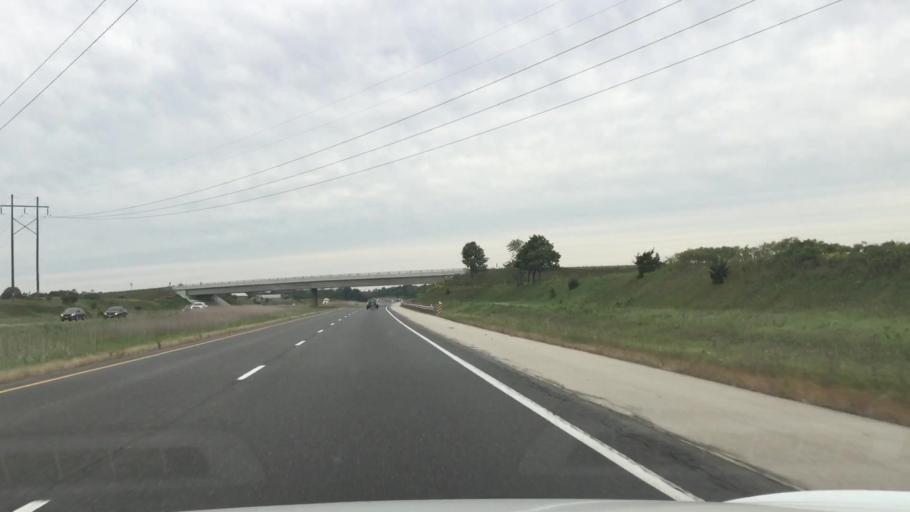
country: CA
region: Ontario
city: Delaware
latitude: 42.8906
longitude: -81.3575
